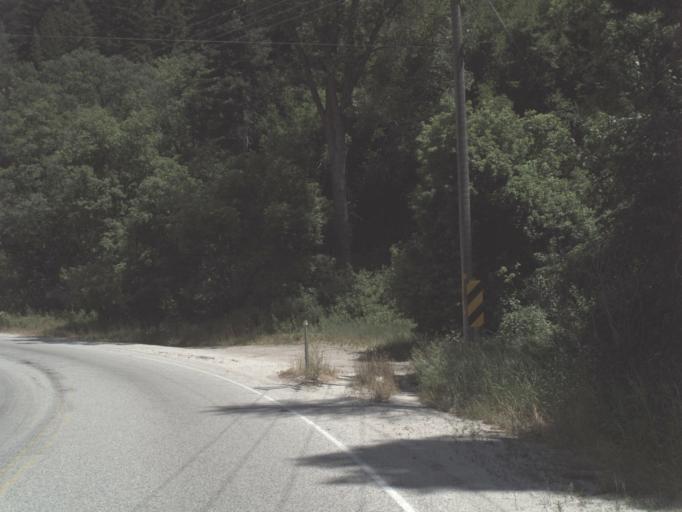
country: US
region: Utah
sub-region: Weber County
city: Liberty
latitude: 41.2488
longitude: -111.8867
